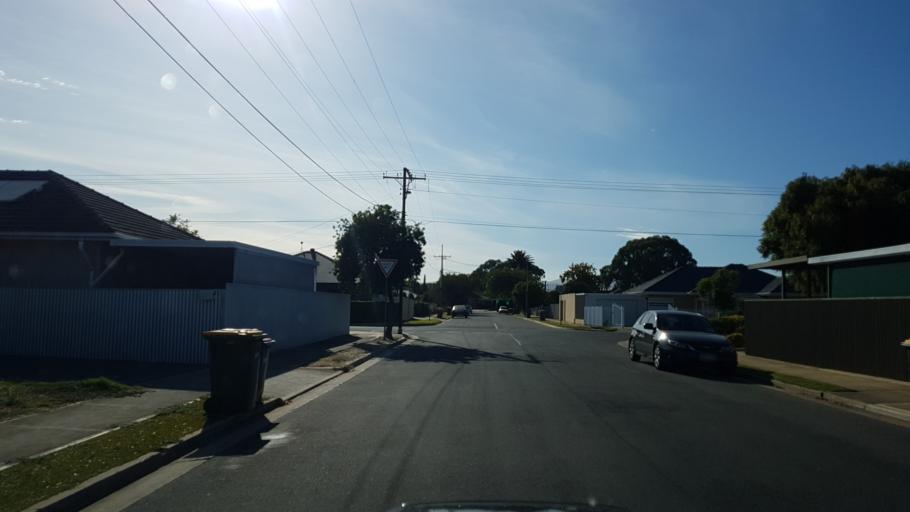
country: AU
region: South Australia
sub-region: City of West Torrens
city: Plympton
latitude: -34.9589
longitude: 138.5471
